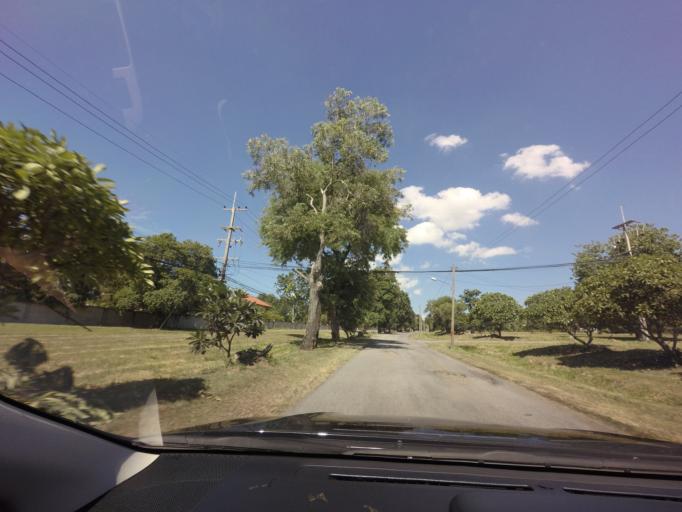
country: TH
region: Chon Buri
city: Bang Lamung
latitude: 13.1052
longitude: 100.9267
